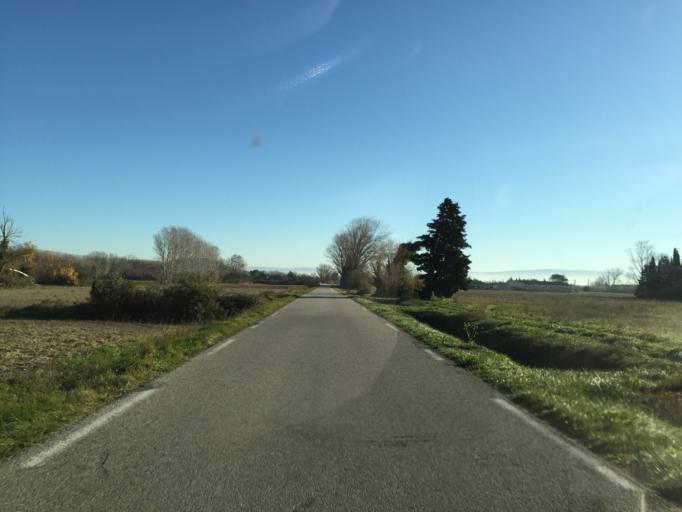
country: FR
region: Provence-Alpes-Cote d'Azur
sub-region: Departement du Vaucluse
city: Entraigues-sur-la-Sorgue
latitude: 44.0205
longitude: 4.9213
